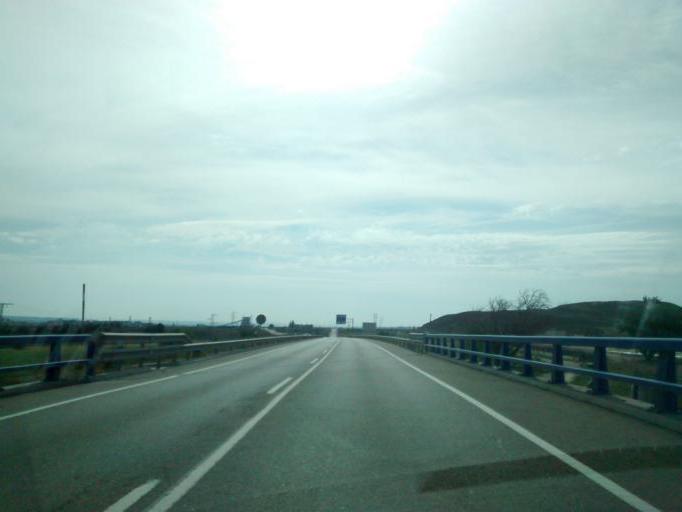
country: ES
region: Aragon
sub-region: Provincia de Zaragoza
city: El Burgo de Ebro
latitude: 41.5483
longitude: -0.7055
